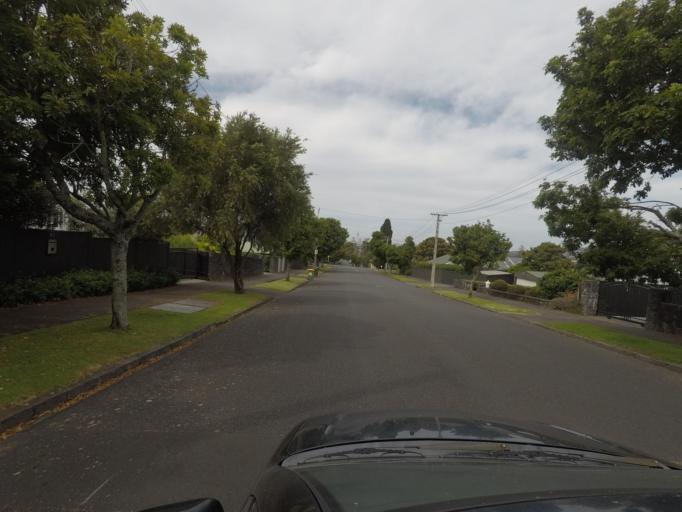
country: NZ
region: Auckland
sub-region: Auckland
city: Auckland
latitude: -36.8859
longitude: 174.7204
